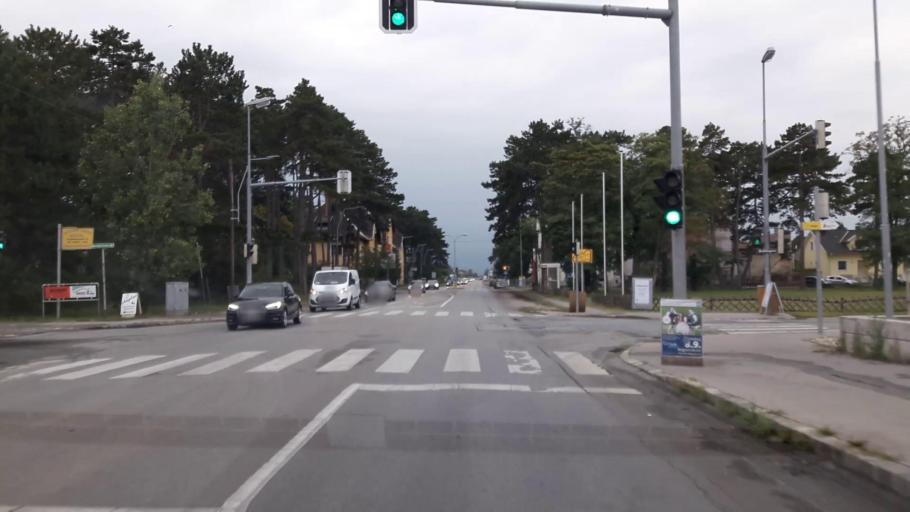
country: AT
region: Lower Austria
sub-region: Politischer Bezirk Ganserndorf
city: Strasshof an der Nordbahn
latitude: 48.3158
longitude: 16.6342
